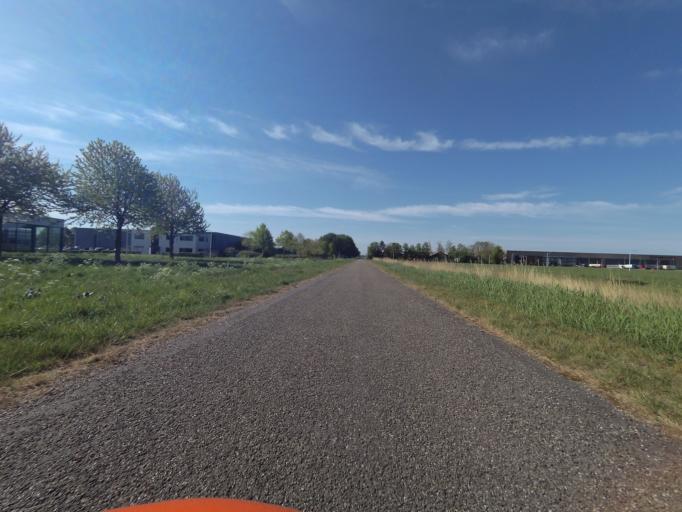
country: NL
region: Flevoland
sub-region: Gemeente Dronten
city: Dronten
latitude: 52.5462
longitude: 5.7043
